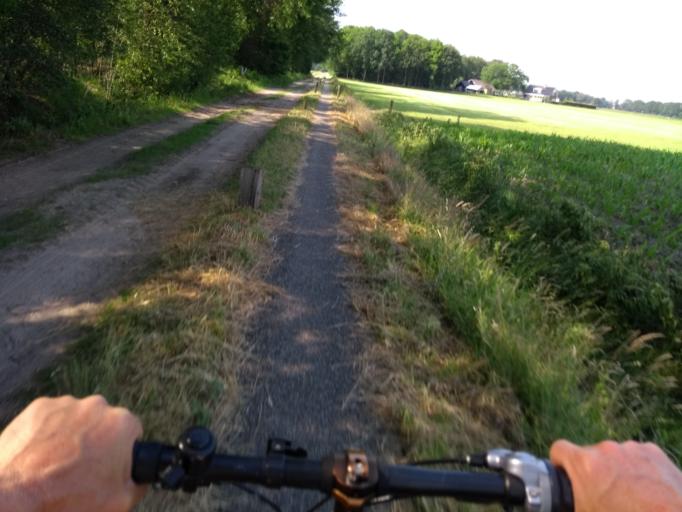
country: NL
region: Overijssel
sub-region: Gemeente Borne
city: Borne
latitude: 52.3543
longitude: 6.7270
